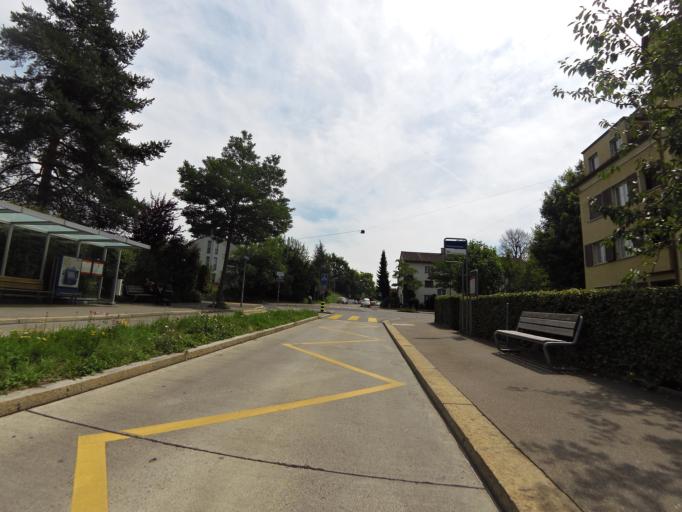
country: CH
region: Zurich
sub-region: Bezirk Zuerich
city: Zuerich (Kreis 2) / Wollishofen
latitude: 47.3369
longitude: 8.5328
